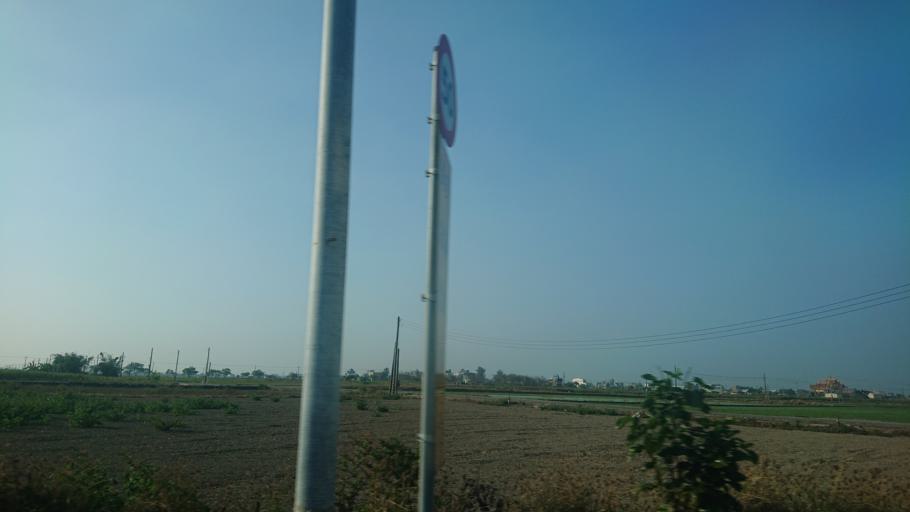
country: TW
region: Taiwan
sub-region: Tainan
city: Tainan
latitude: 23.1286
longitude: 120.2298
